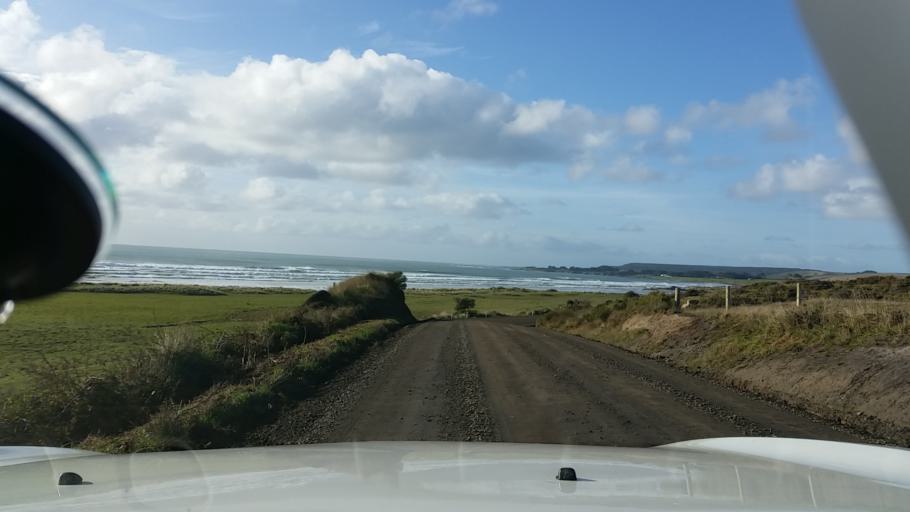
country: NZ
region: Chatham Islands
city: Waitangi
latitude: -44.0101
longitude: -176.3990
